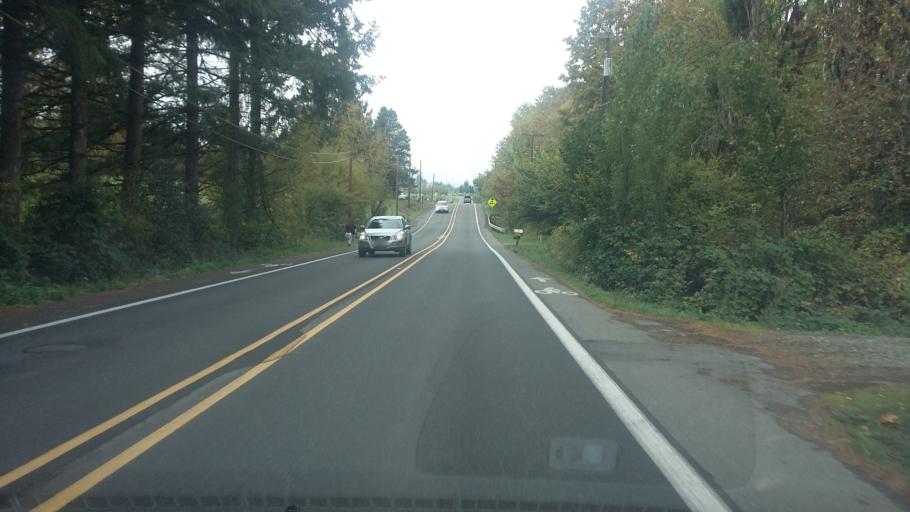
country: US
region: Washington
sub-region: Clark County
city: Ridgefield
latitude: 45.8158
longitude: -122.6937
